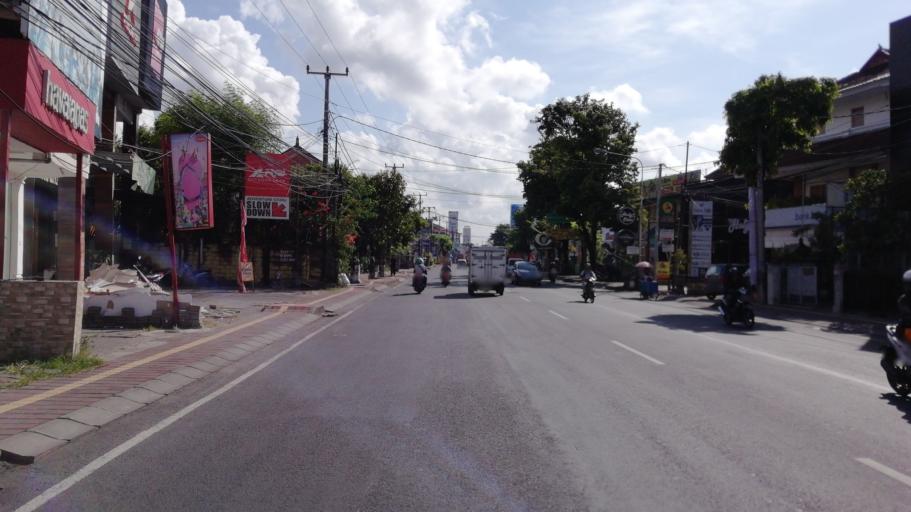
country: ID
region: Bali
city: Denpasar
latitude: -8.6729
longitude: 115.2083
